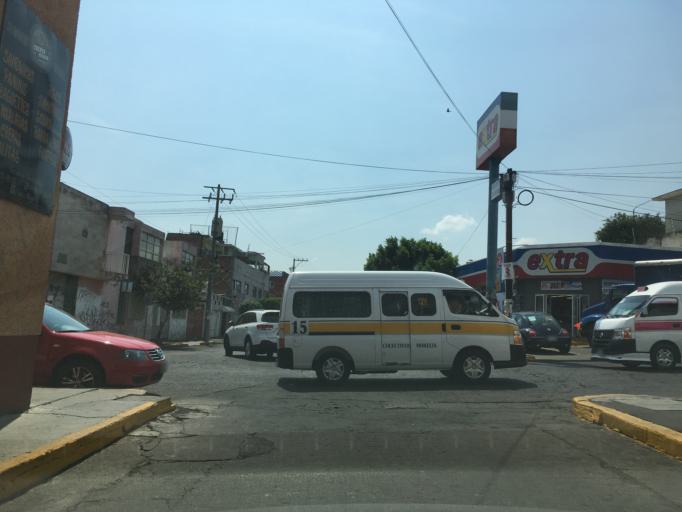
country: MX
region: Michoacan
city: Morelia
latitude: 19.7032
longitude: -101.1778
